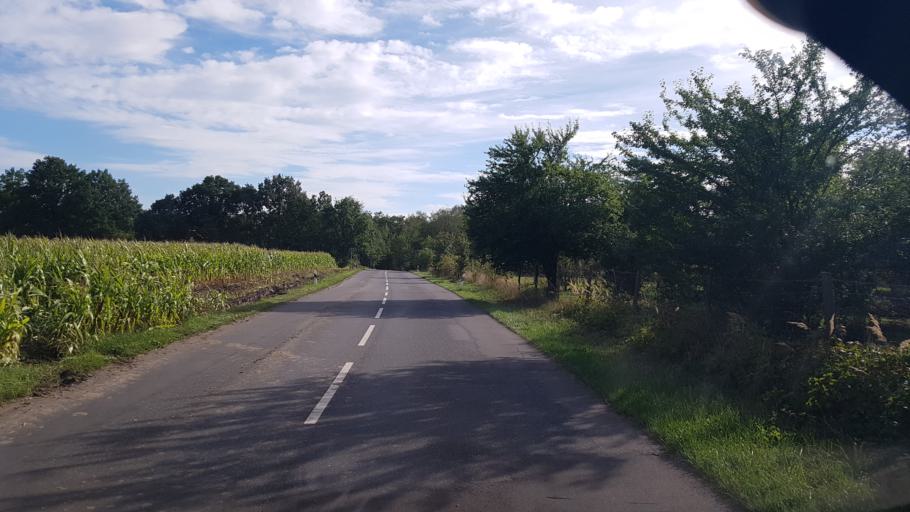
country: DE
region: Brandenburg
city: Spremberg
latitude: 51.5547
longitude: 14.3188
